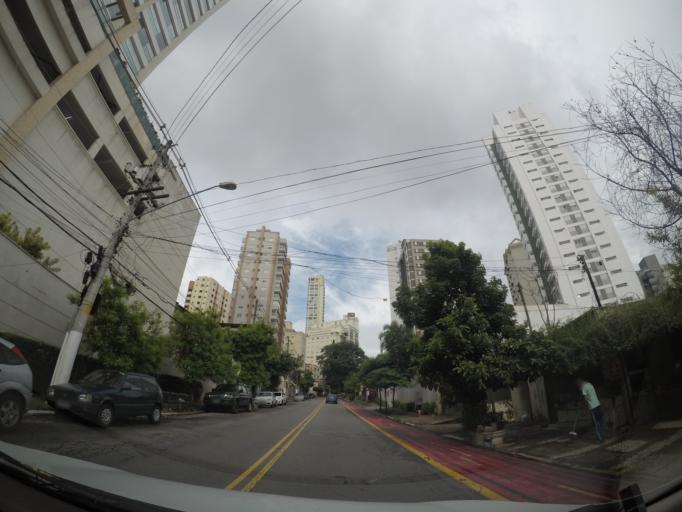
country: BR
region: Sao Paulo
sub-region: Sao Paulo
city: Sao Paulo
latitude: -23.5897
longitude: -46.6257
